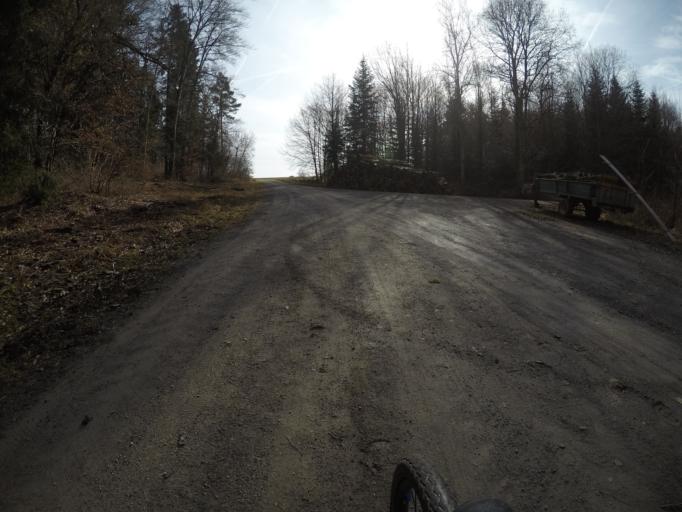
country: DE
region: Baden-Wuerttemberg
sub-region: Regierungsbezirk Stuttgart
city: Oberjettingen
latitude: 48.5883
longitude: 8.7945
